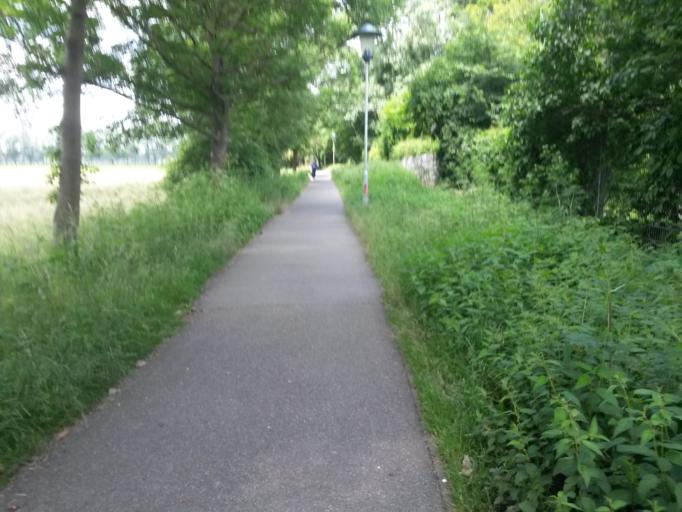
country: DE
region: Bavaria
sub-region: Regierungsbezirk Mittelfranken
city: Furth
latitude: 49.4731
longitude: 11.0085
